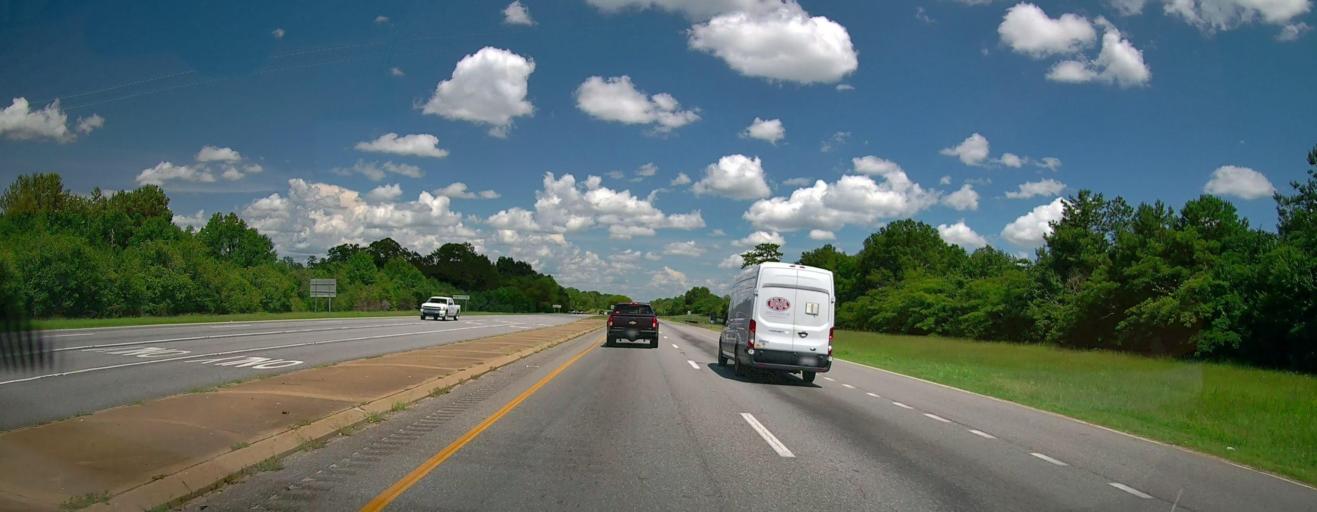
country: US
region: Alabama
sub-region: Montgomery County
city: Montgomery
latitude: 32.4226
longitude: -86.2673
